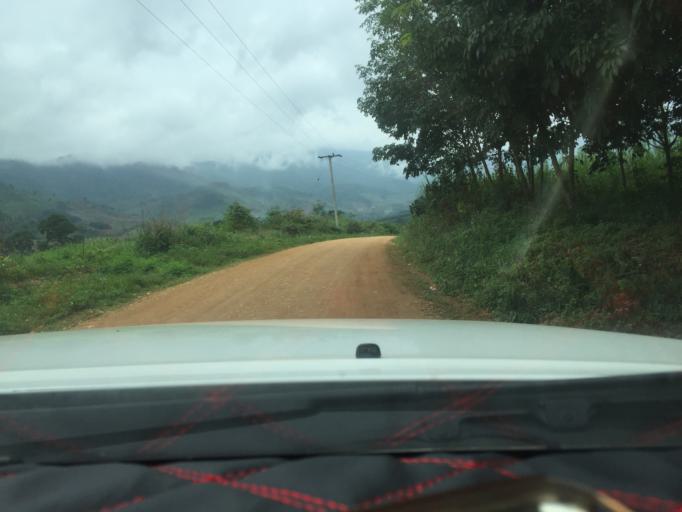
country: TH
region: Phayao
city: Phu Sang
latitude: 19.7408
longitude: 100.4616
